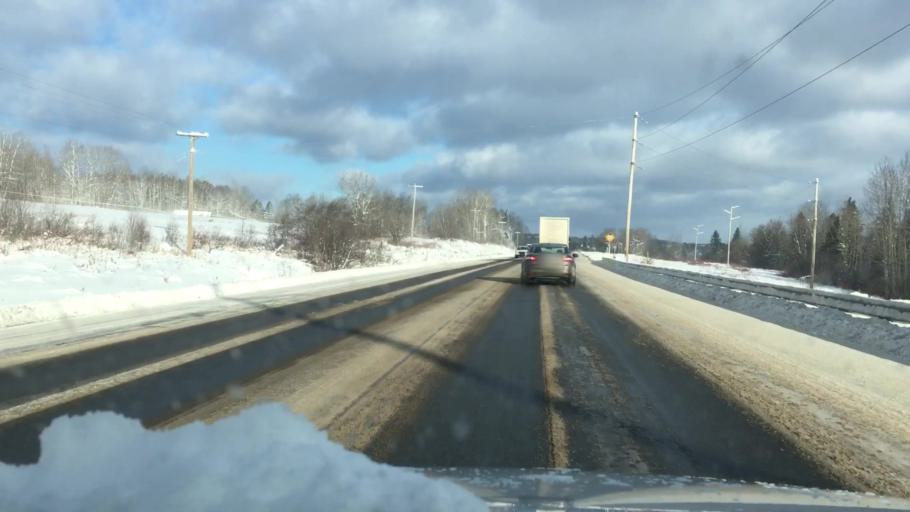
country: US
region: Maine
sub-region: Aroostook County
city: Caribou
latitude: 46.8429
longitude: -68.0032
